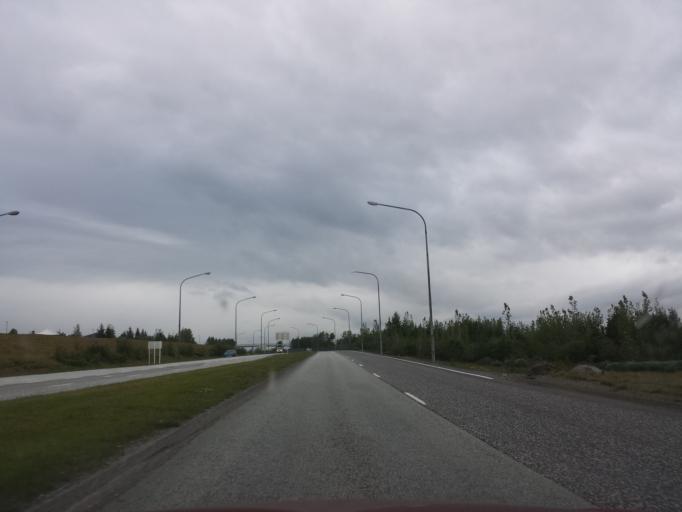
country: IS
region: Capital Region
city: Hafnarfjoerdur
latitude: 64.0840
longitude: -21.9432
